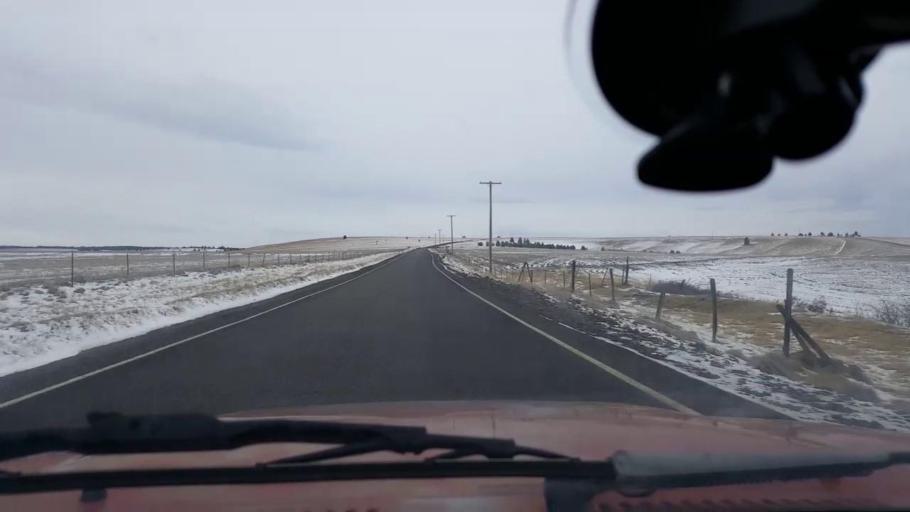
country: US
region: Washington
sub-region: Garfield County
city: Pomeroy
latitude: 46.3202
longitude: -117.3921
